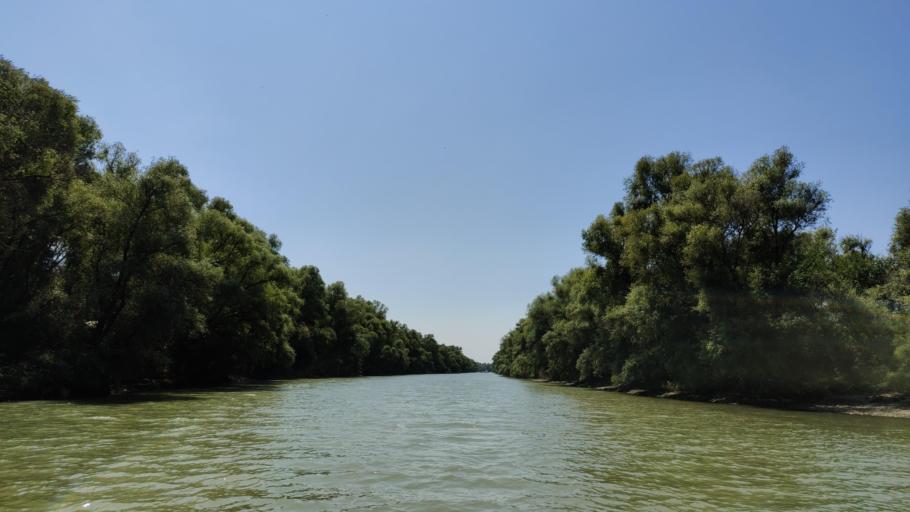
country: RO
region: Tulcea
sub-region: Comuna Pardina
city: Pardina
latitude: 45.2521
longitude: 28.9255
